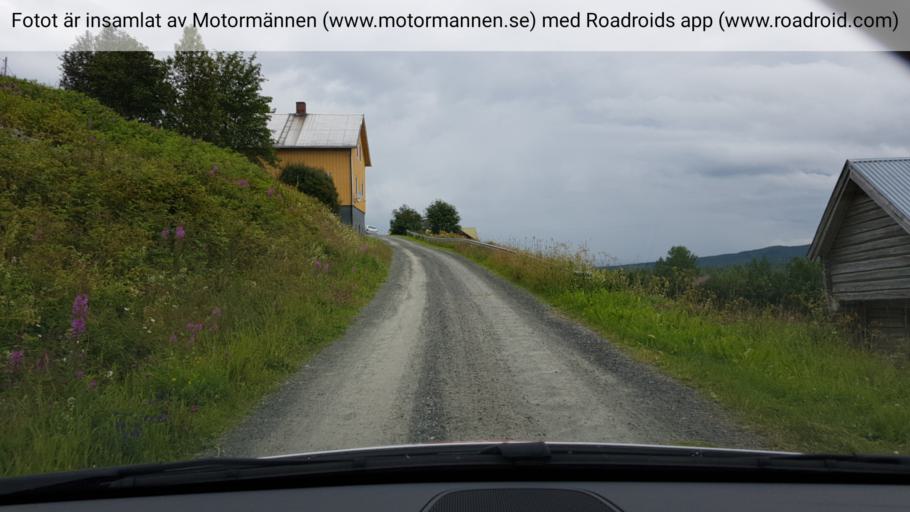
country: SE
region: Jaemtland
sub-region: Krokoms Kommun
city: Valla
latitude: 63.5826
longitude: 13.9872
